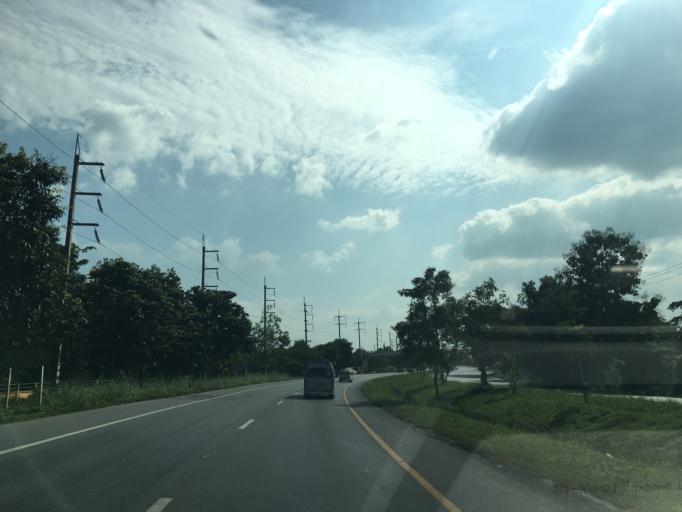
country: TH
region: Chiang Rai
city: Mae Lao
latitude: 19.7093
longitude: 99.7203
